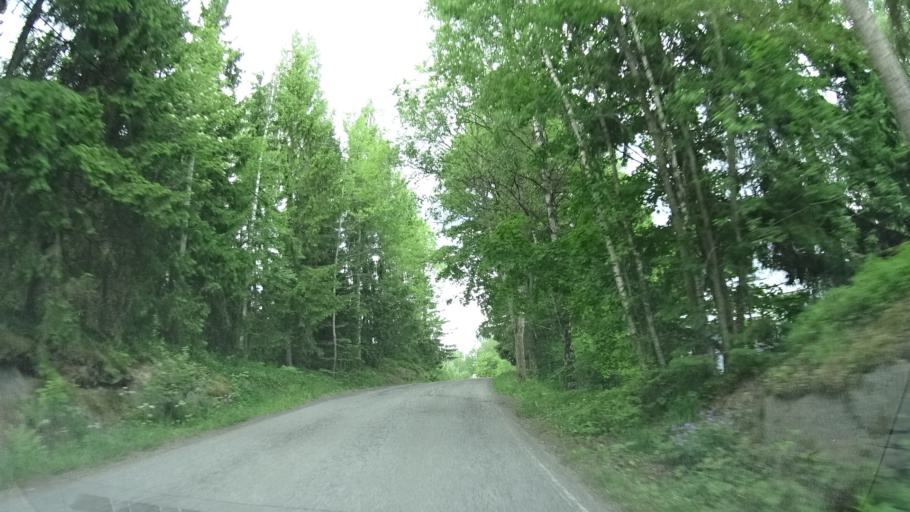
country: FI
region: Uusimaa
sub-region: Helsinki
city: Siuntio
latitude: 60.2097
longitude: 24.2376
